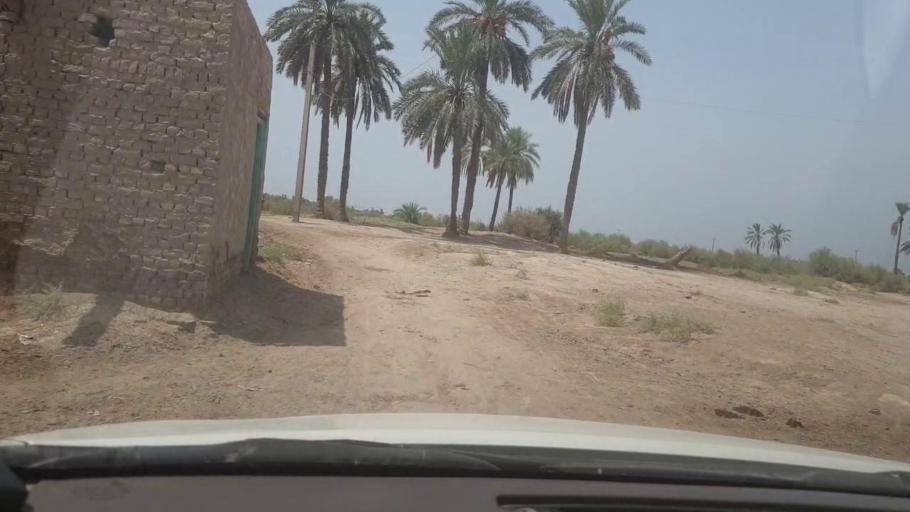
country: PK
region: Sindh
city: Garhi Yasin
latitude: 27.9807
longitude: 68.5430
